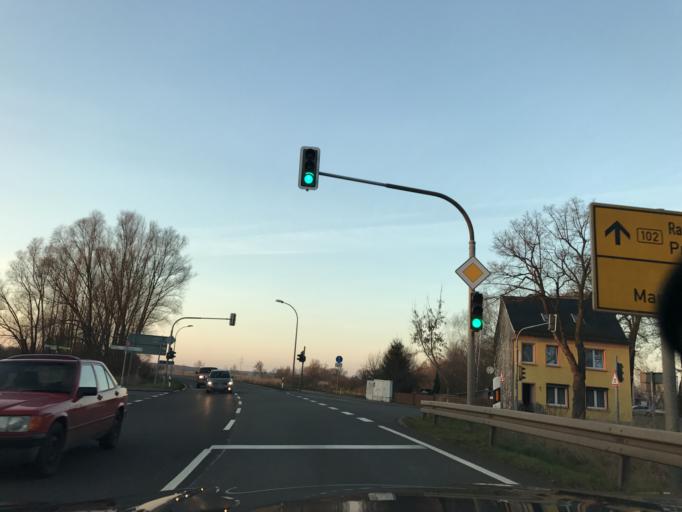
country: DE
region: Brandenburg
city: Nennhausen
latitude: 52.4982
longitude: 12.4589
